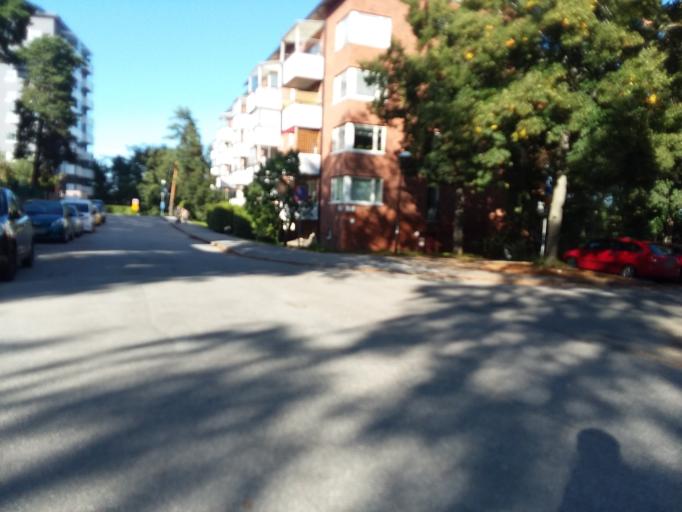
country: SE
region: Stockholm
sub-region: Stockholms Kommun
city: Bromma
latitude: 59.3464
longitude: 17.8891
